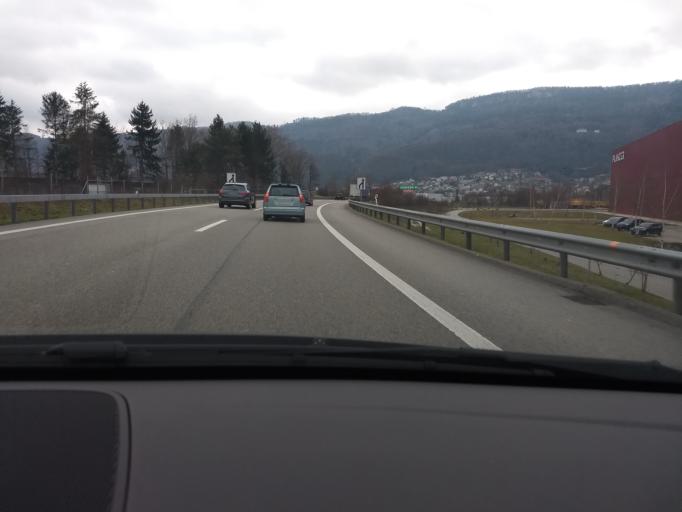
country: CH
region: Solothurn
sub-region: Bezirk Olten
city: Gunzgen
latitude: 47.3130
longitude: 7.8086
